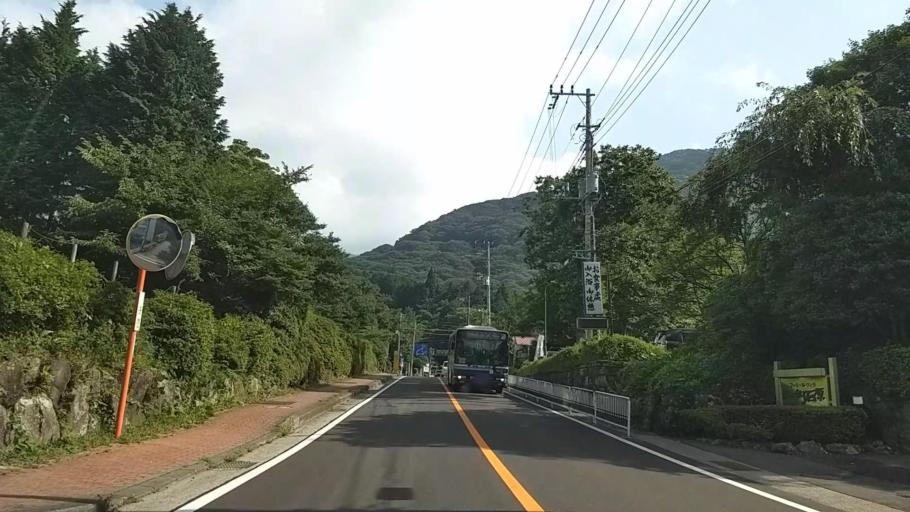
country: JP
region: Kanagawa
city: Hakone
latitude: 35.2656
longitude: 139.0135
